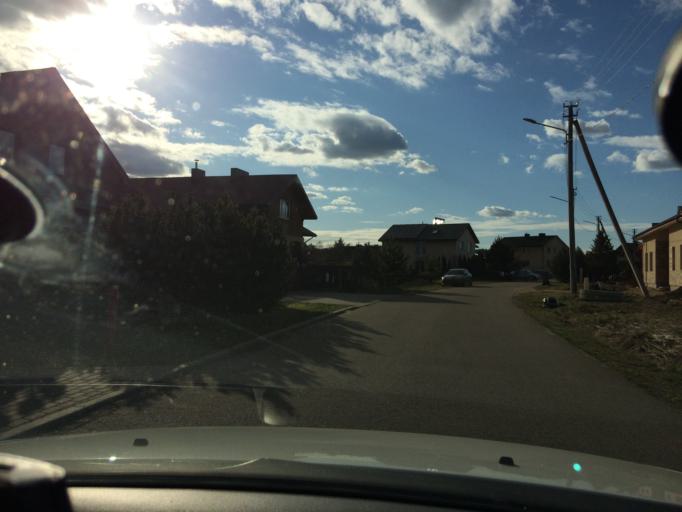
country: LT
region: Vilnius County
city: Rasos
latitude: 54.7759
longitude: 25.3493
